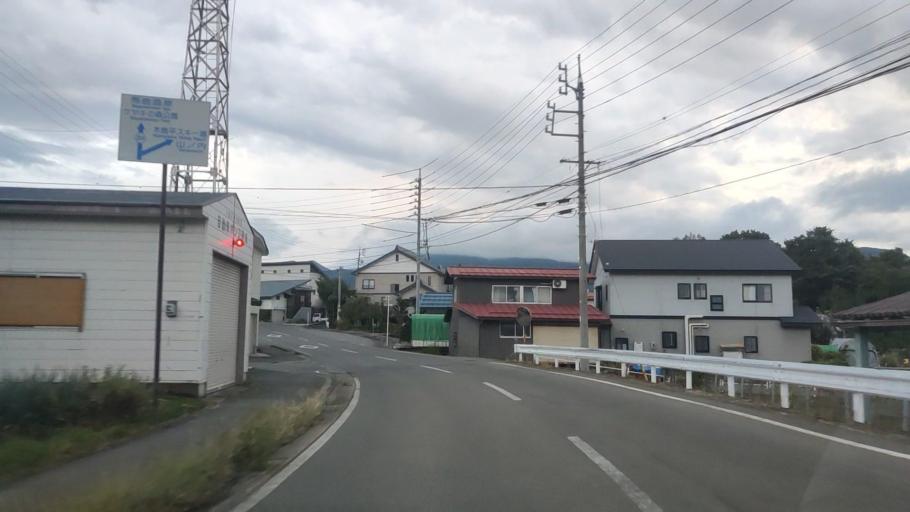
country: JP
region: Nagano
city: Iiyama
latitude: 36.8556
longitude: 138.4088
